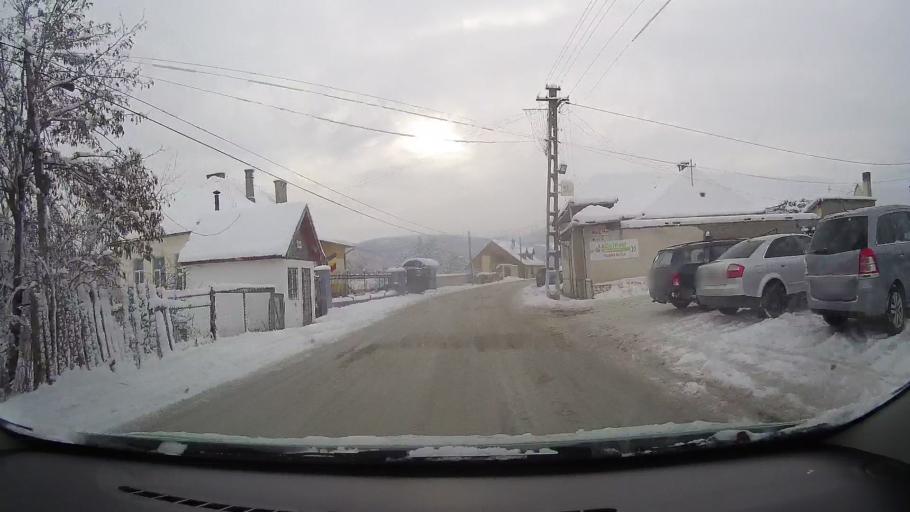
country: RO
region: Alba
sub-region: Comuna Pianu
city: Pianu de Jos
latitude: 45.9353
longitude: 23.4862
